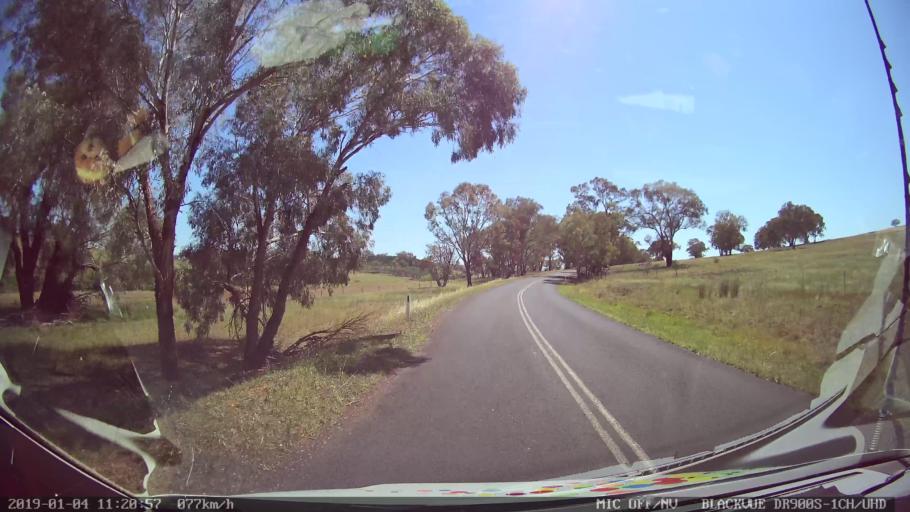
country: AU
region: New South Wales
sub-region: Cabonne
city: Molong
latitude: -33.1583
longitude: 148.7060
